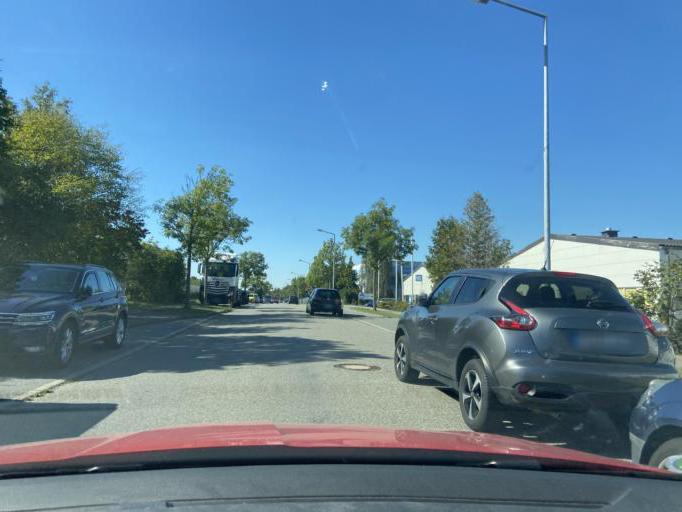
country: DE
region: Saxony
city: Ottendorf-Okrilla
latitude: 51.1823
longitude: 13.8406
